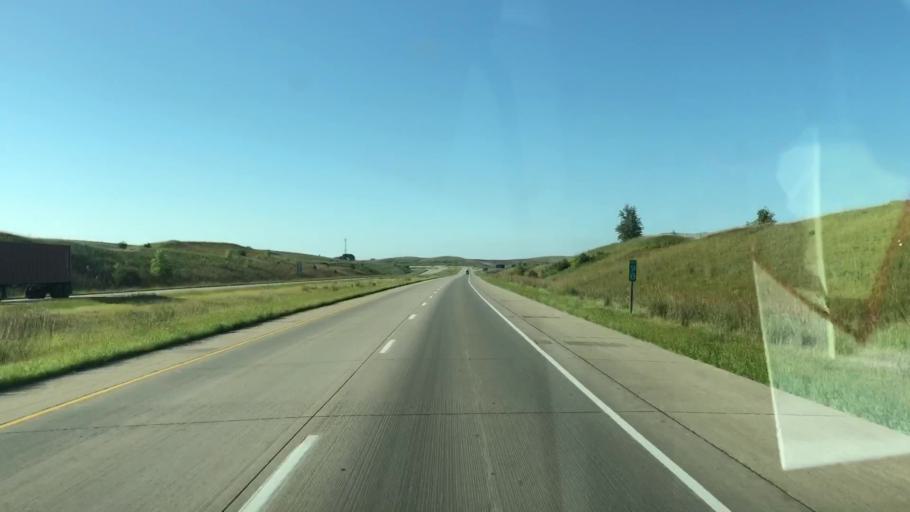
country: US
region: Iowa
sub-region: Woodbury County
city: Sioux City
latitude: 42.5306
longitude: -96.3391
